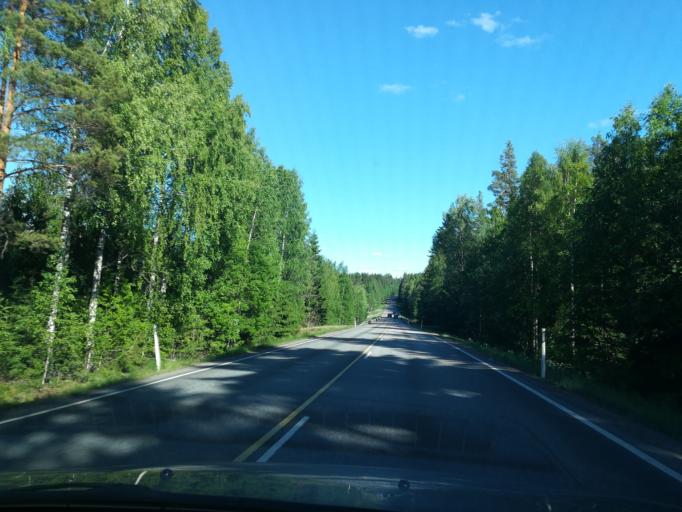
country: FI
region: South Karelia
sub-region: Imatra
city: Ruokolahti
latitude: 61.3589
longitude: 28.7068
